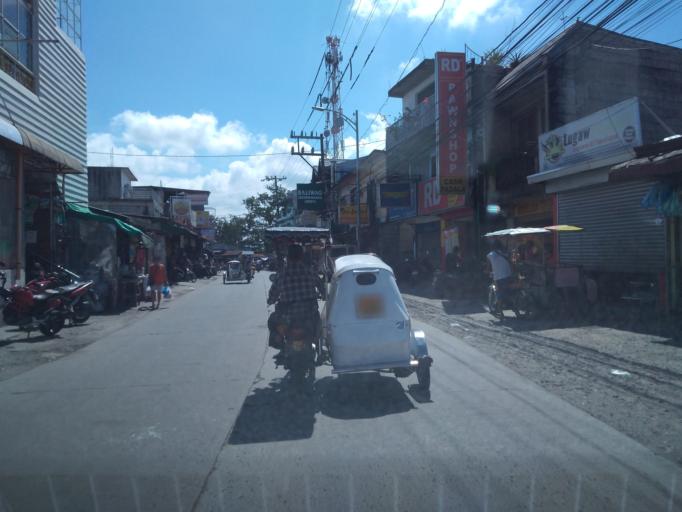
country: PH
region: Central Luzon
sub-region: Province of Bulacan
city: Bitungol
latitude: 14.8578
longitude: 121.0545
